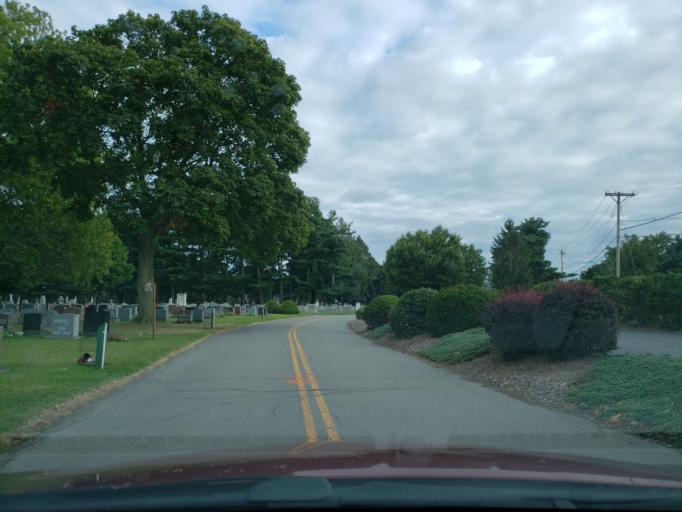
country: US
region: New York
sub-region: Monroe County
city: Greece
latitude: 43.2132
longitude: -77.6384
